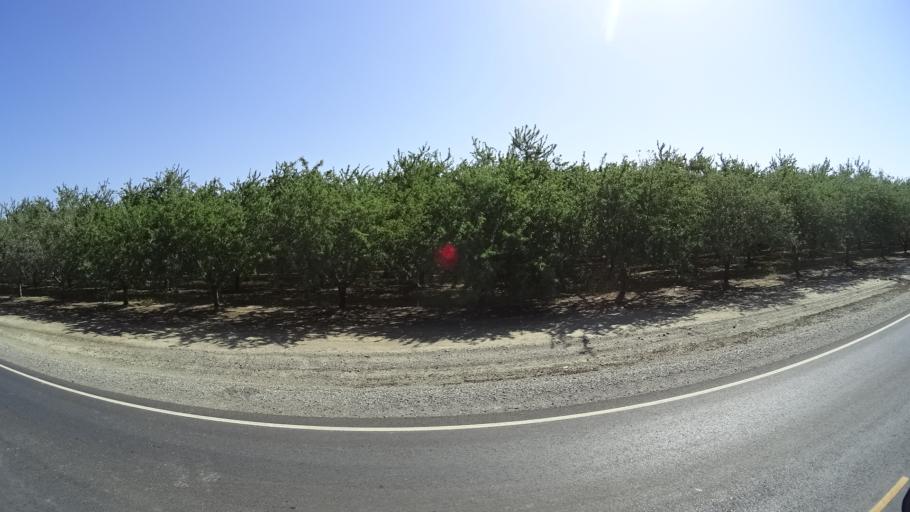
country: US
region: California
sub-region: Glenn County
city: Hamilton City
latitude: 39.6554
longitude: -122.0649
